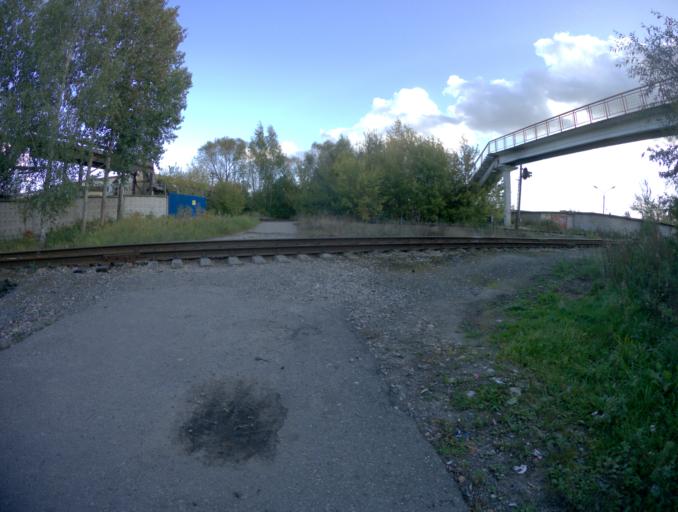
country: RU
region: Moskovskaya
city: Shatura
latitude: 55.5735
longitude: 39.5543
